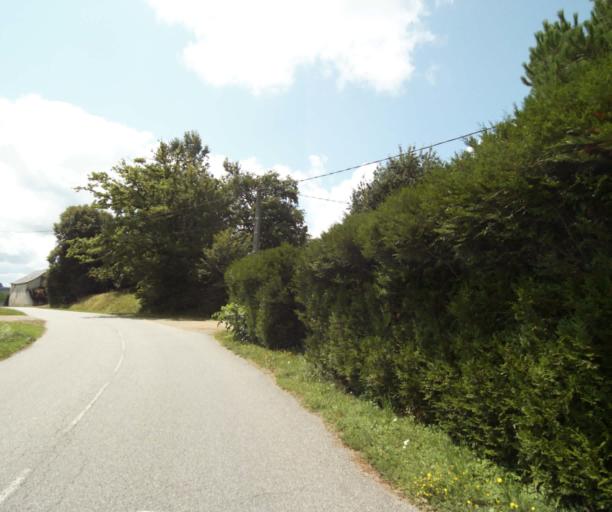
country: FR
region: Limousin
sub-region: Departement de la Correze
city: Sainte-Fortunade
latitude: 45.2001
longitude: 1.8401
